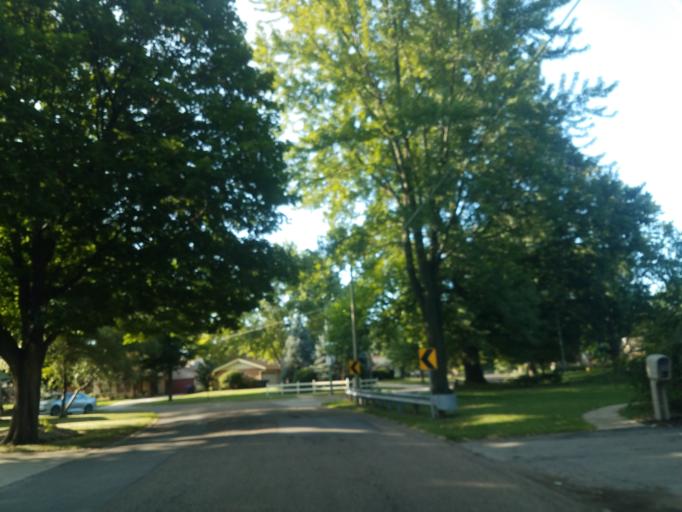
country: US
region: Illinois
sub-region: McLean County
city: Bloomington
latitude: 40.4845
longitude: -88.9815
